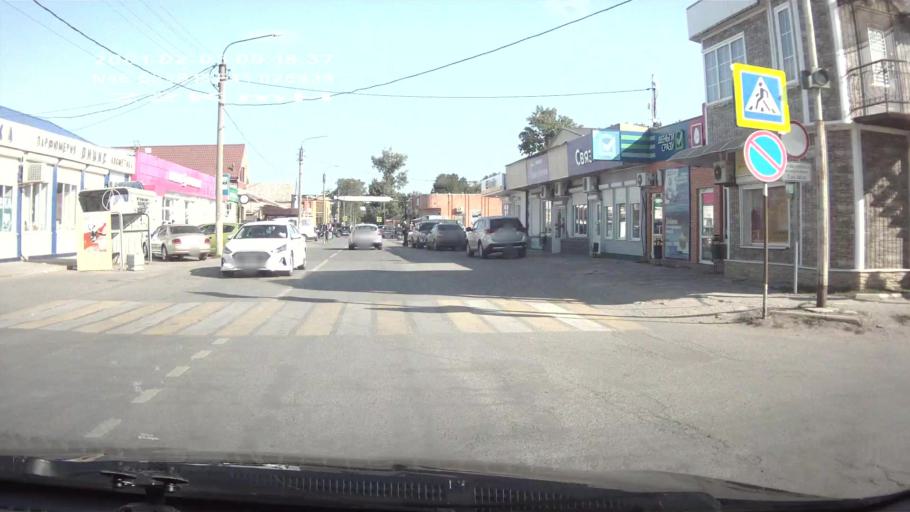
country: RU
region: Rostov
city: Tselina
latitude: 46.5359
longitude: 41.0268
